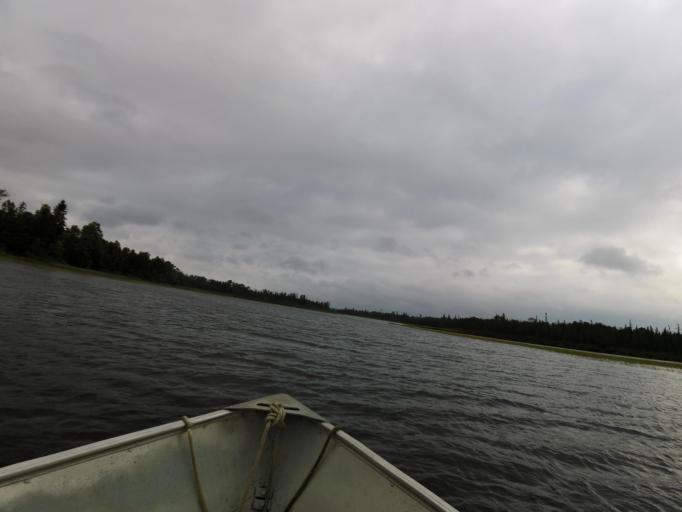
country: CA
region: Ontario
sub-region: Rainy River District
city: Atikokan
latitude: 49.5891
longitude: -91.3678
